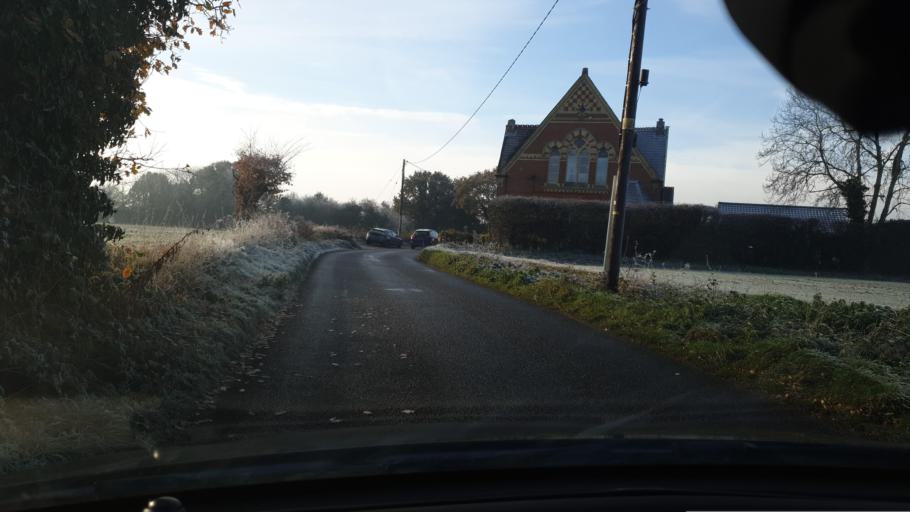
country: GB
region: England
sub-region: Essex
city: Mistley
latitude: 51.9905
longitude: 1.1033
